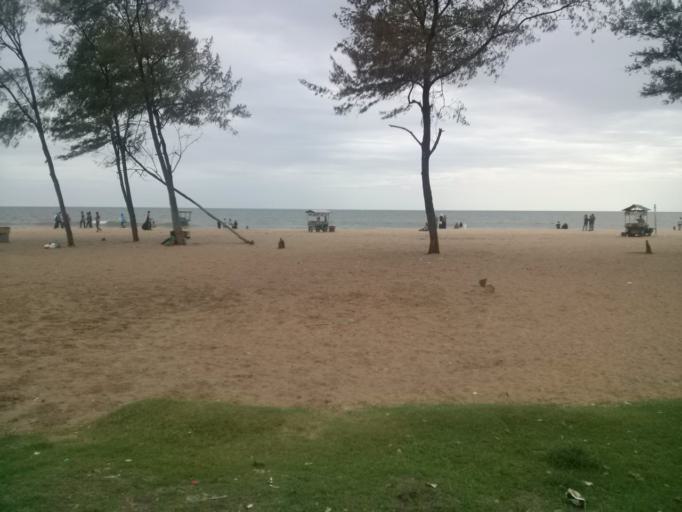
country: IN
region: Kerala
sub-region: Kozhikode
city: Kozhikode
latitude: 11.2574
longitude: 75.7694
